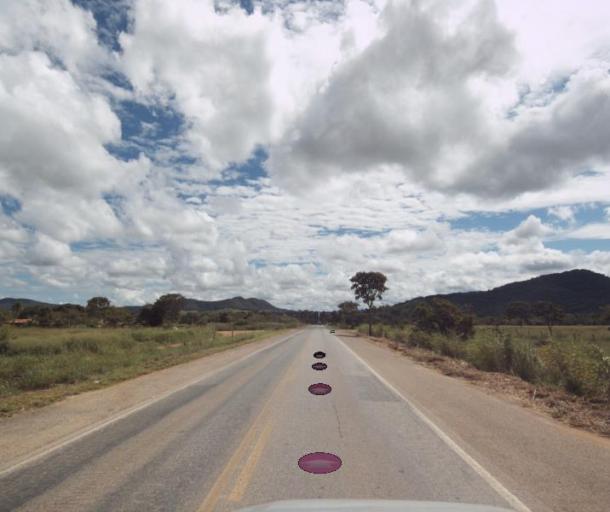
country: BR
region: Goias
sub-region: Uruacu
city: Uruacu
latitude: -14.4281
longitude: -49.1570
